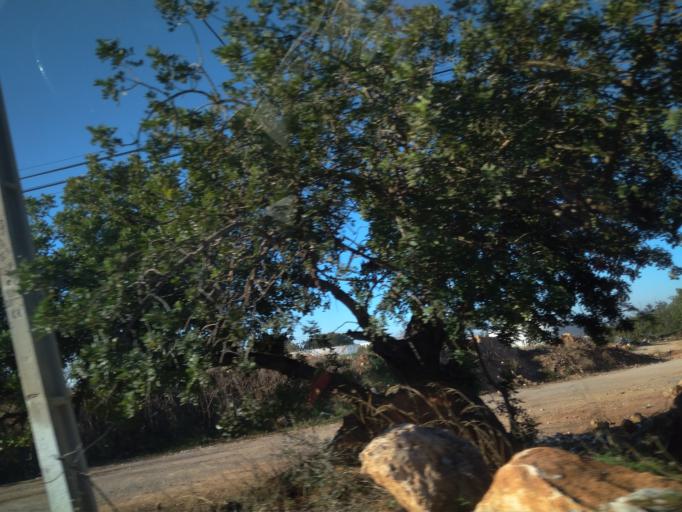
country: PT
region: Faro
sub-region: Faro
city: Santa Barbara de Nexe
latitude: 37.0921
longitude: -7.9620
